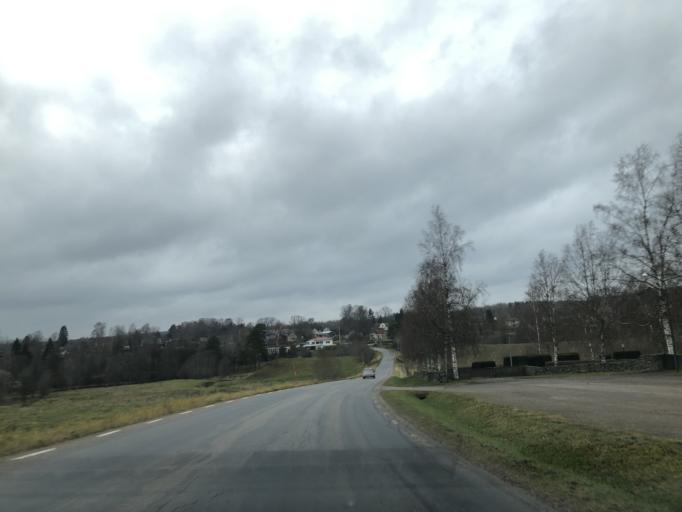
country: SE
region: Vaestra Goetaland
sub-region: Ulricehamns Kommun
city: Ulricehamn
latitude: 57.8993
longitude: 13.4773
